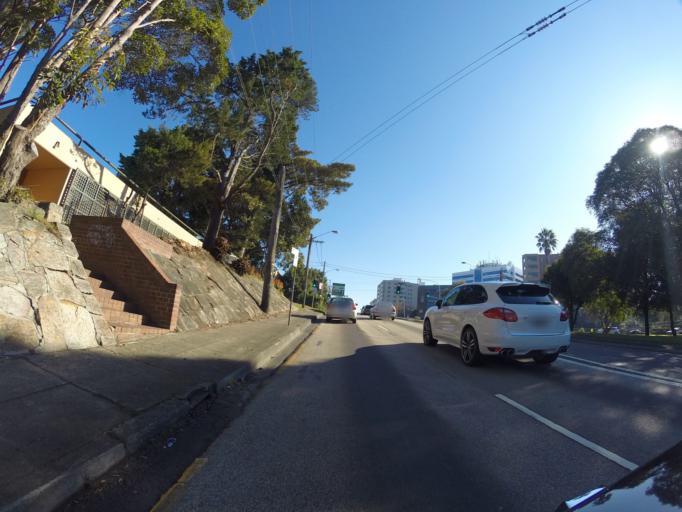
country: AU
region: New South Wales
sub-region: Hurstville
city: Penshurst
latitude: -33.9661
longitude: 151.0949
